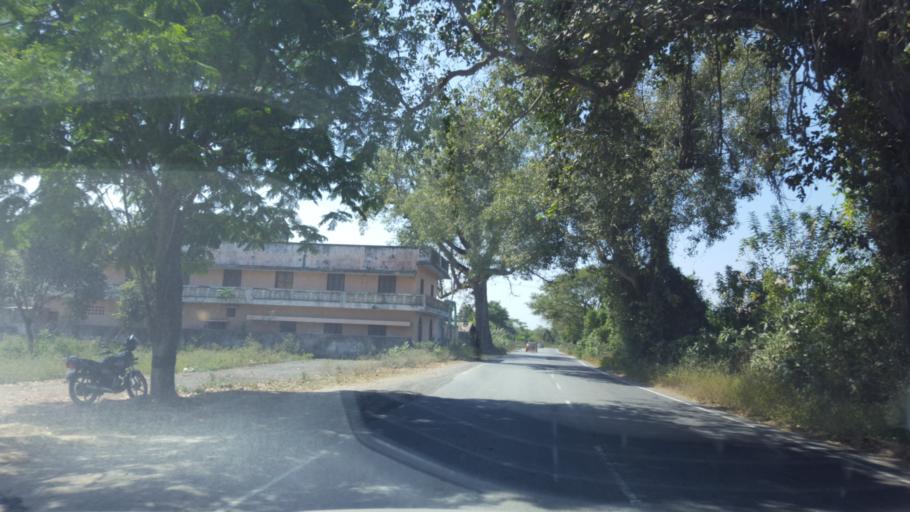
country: IN
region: Tamil Nadu
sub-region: Kancheepuram
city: Wallajahbad
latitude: 12.7811
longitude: 79.8476
